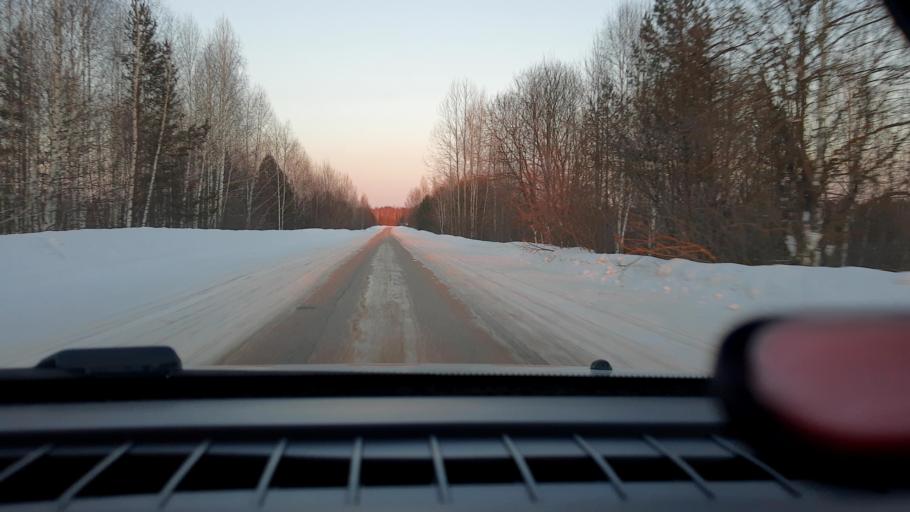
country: RU
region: Nizjnij Novgorod
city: Lyskovo
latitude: 56.1622
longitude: 45.1921
